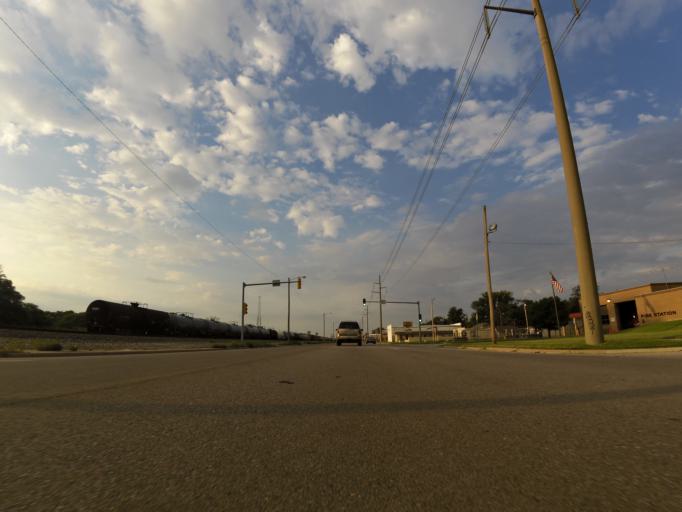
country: US
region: Kansas
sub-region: Sedgwick County
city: Wichita
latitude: 37.7430
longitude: -97.3360
